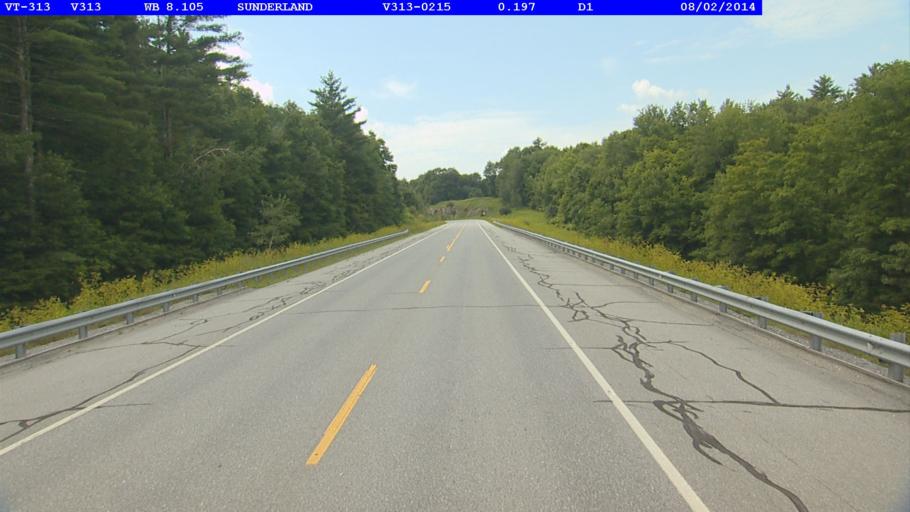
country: US
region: Vermont
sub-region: Bennington County
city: Arlington
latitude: 43.0514
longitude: -73.1361
